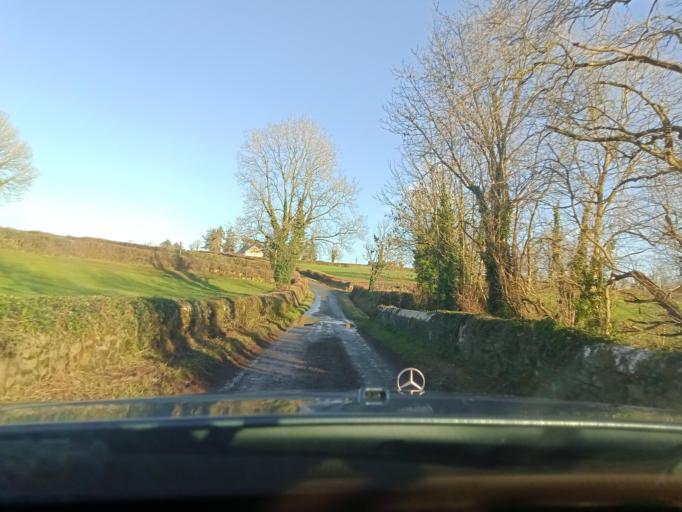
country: IE
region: Munster
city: Carrick-on-Suir
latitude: 52.4394
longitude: -7.3935
